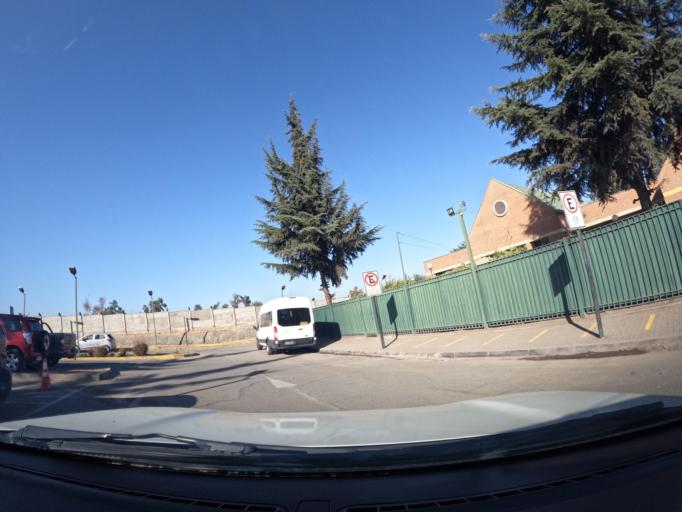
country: CL
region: Santiago Metropolitan
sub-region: Provincia de Santiago
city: Villa Presidente Frei, Nunoa, Santiago, Chile
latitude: -33.4979
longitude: -70.5466
